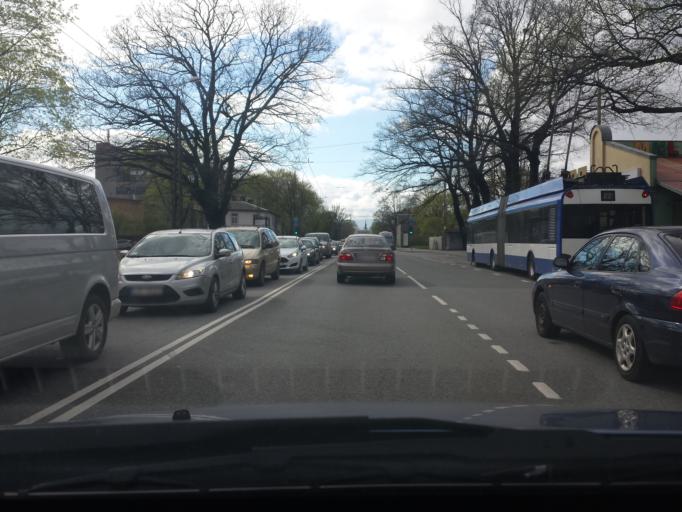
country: LV
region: Riga
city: Riga
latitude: 56.9509
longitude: 24.1731
